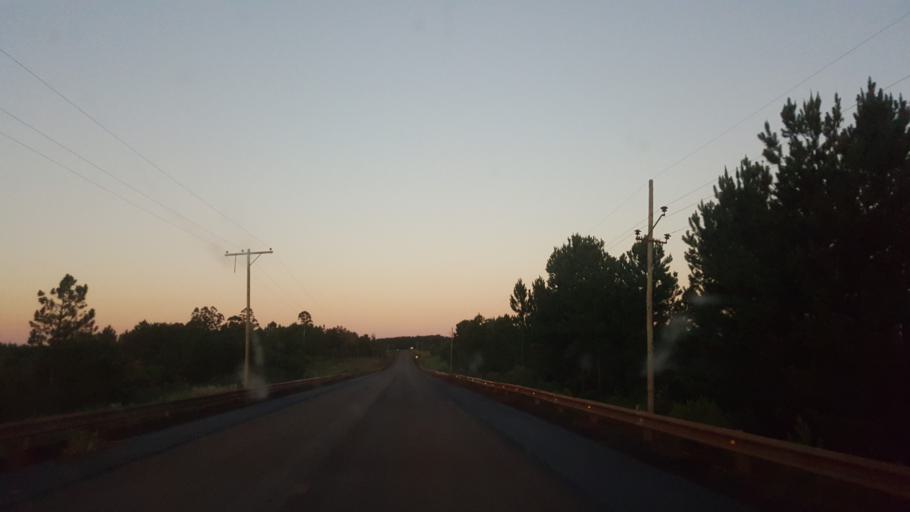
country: AR
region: Corrientes
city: Garruchos
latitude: -28.2319
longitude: -55.8111
